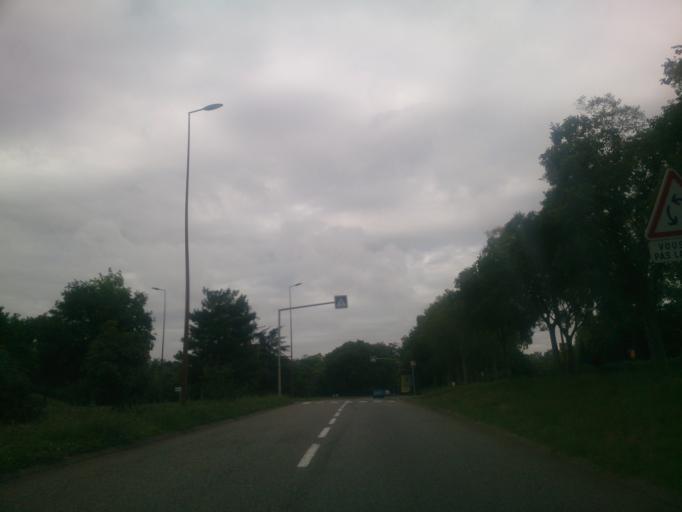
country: FR
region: Midi-Pyrenees
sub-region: Departement de la Haute-Garonne
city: Portet-sur-Garonne
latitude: 43.5746
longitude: 1.3979
